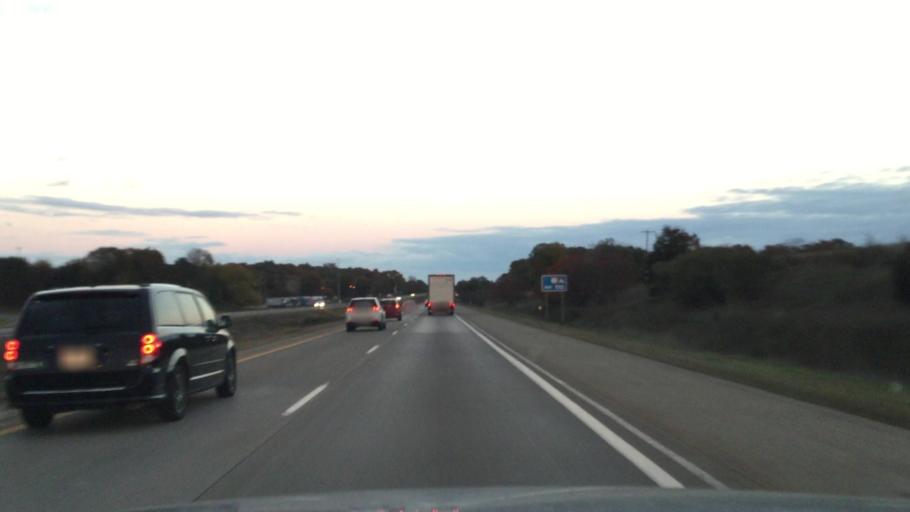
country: US
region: Michigan
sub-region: Jackson County
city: Grass Lake
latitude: 42.2920
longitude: -84.2207
